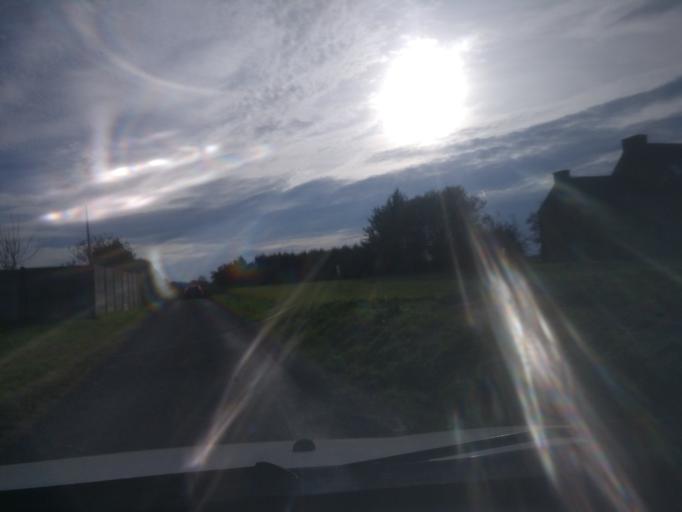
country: FR
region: Brittany
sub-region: Departement d'Ille-et-Vilaine
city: Cancale
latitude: 48.6753
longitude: -1.8718
